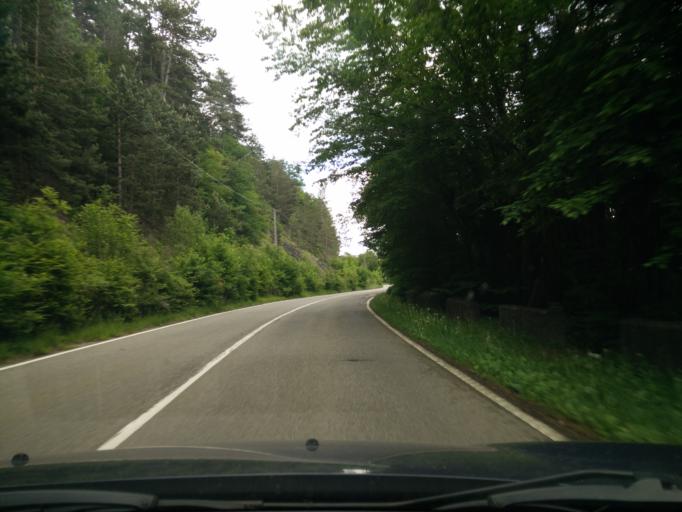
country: FR
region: Champagne-Ardenne
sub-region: Departement des Ardennes
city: Vireux-Molhain
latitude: 50.0772
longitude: 4.6139
